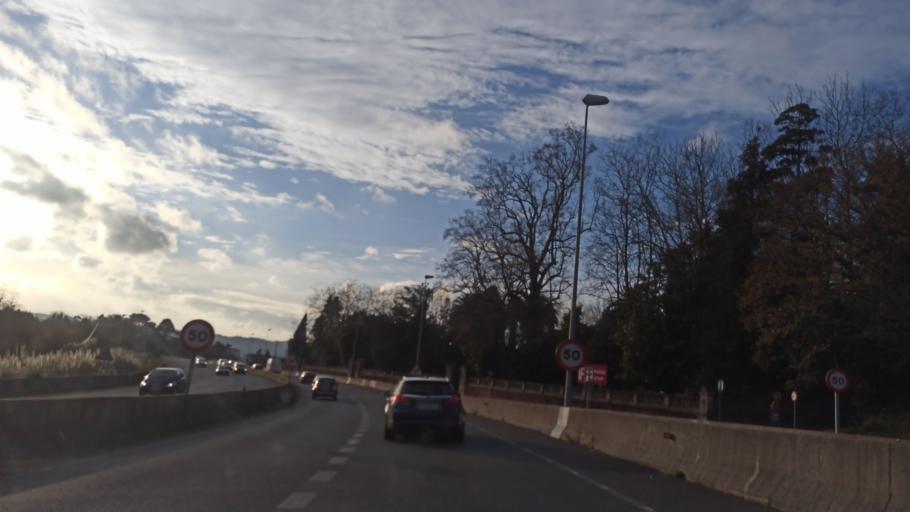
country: ES
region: Galicia
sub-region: Provincia da Coruna
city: Oleiros
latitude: 43.3233
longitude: -8.3421
